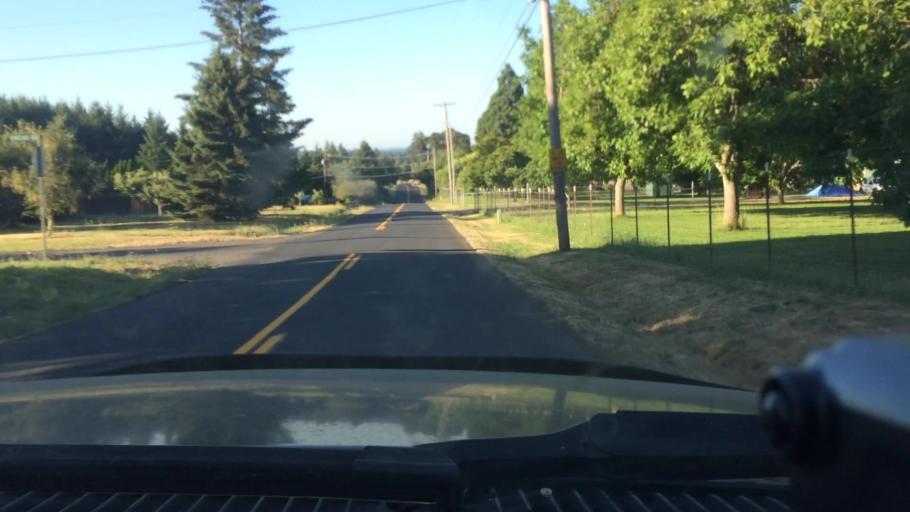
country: US
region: Oregon
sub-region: Yamhill County
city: Newberg
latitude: 45.3267
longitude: -122.9404
